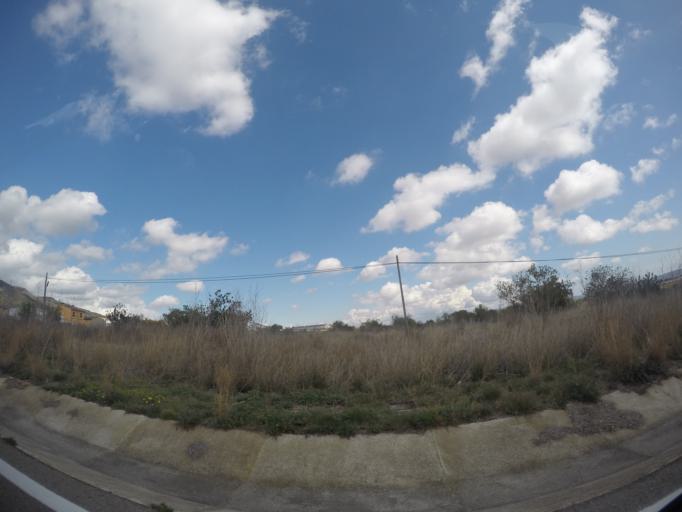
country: ES
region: Catalonia
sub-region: Provincia de Tarragona
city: la Bisbal del Penedes
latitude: 41.2892
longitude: 1.5245
